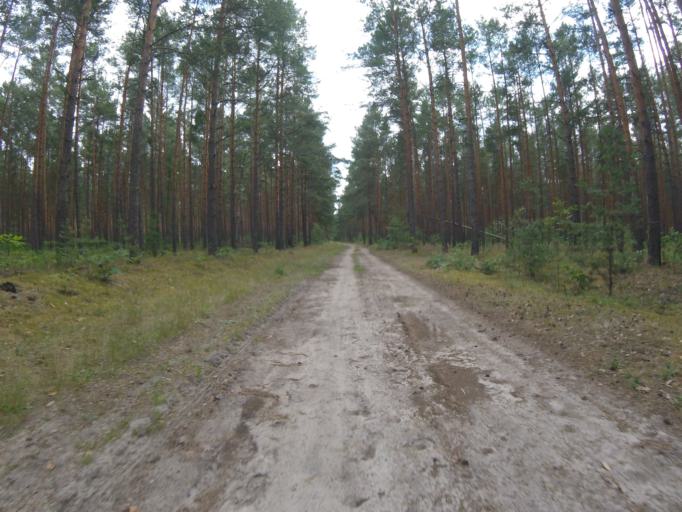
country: DE
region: Brandenburg
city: Halbe
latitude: 52.1348
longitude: 13.6956
